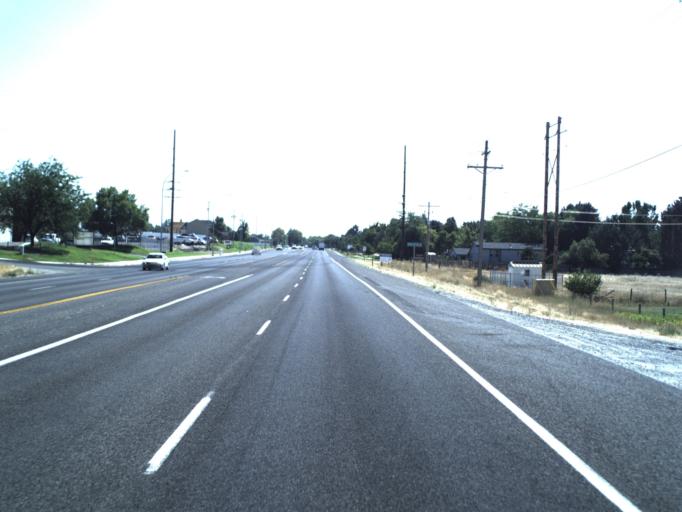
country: US
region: Utah
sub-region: Cache County
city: Smithfield
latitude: 41.8538
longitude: -111.8318
